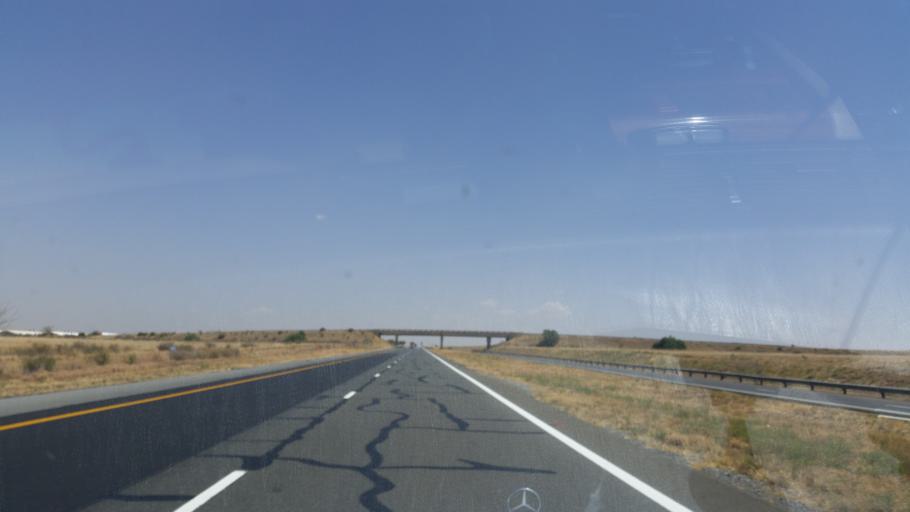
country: ZA
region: Orange Free State
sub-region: Lejweleputswa District Municipality
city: Brandfort
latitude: -28.8654
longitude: 26.5346
